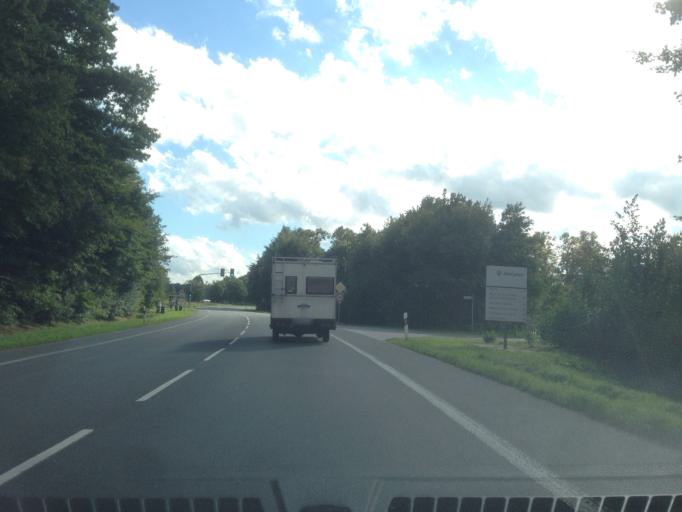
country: DE
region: North Rhine-Westphalia
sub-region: Regierungsbezirk Munster
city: Senden
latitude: 51.8779
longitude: 7.5666
